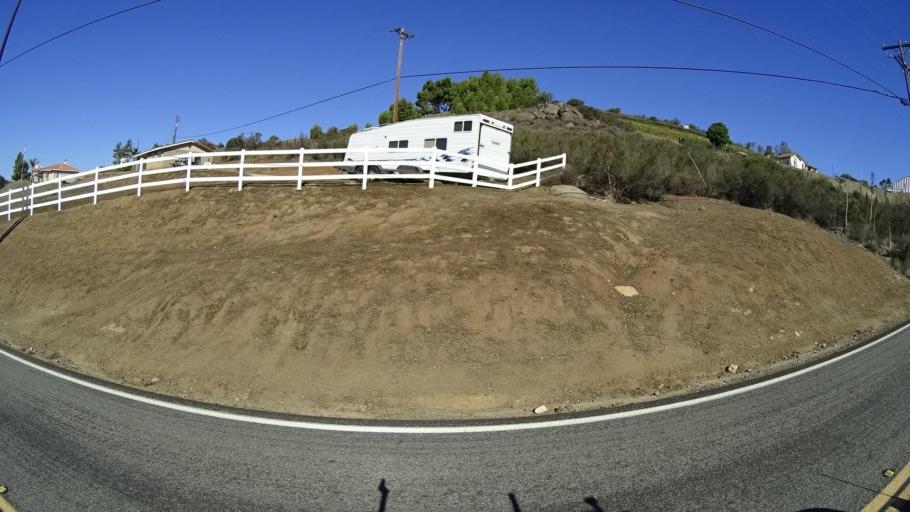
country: US
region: California
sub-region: San Diego County
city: Jamul
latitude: 32.6867
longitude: -116.7503
